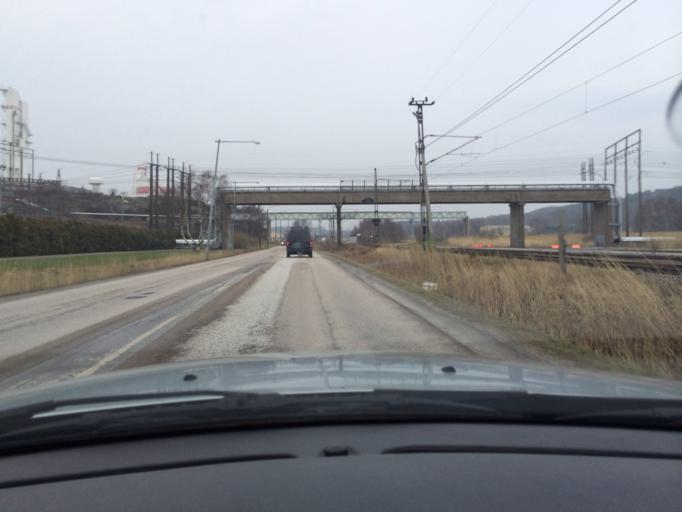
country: SE
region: Vaestra Goetaland
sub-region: Stenungsunds Kommun
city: Stenungsund
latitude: 58.0831
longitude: 11.8304
